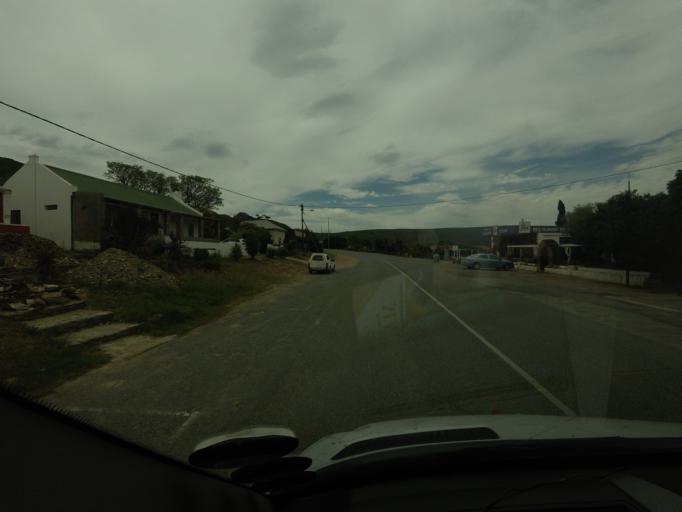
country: ZA
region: Western Cape
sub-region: Overberg District Municipality
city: Swellendam
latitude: -33.9048
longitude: 20.7176
